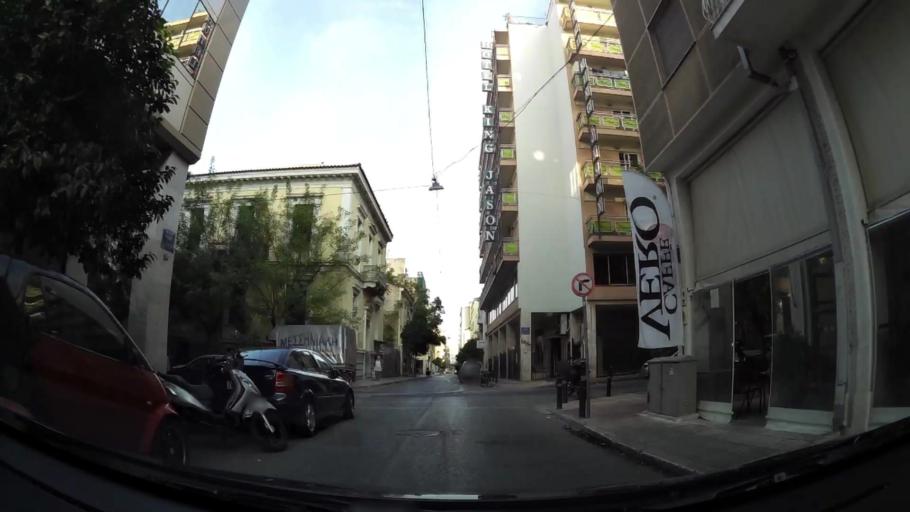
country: GR
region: Attica
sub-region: Nomarchia Athinas
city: Athens
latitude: 37.9831
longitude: 23.7221
